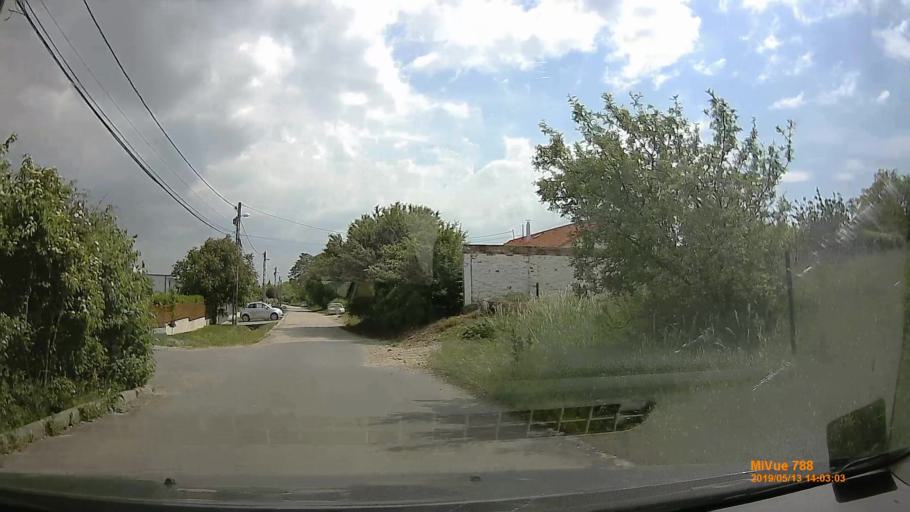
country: HU
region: Budapest
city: Budapest XXII. keruelet
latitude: 47.4247
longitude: 19.0064
